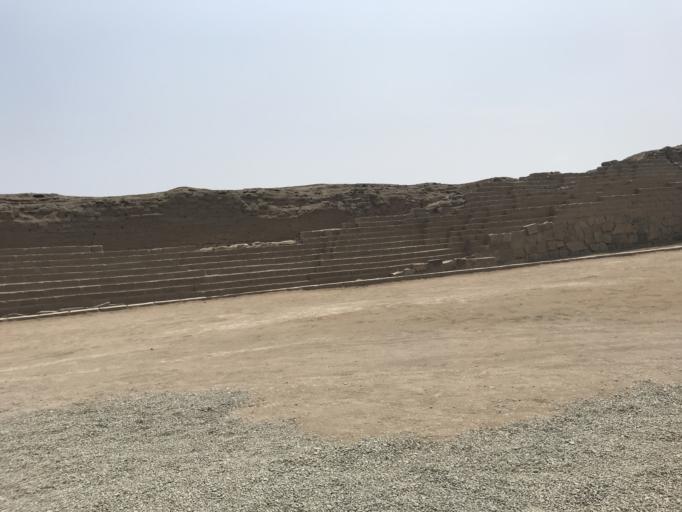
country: PE
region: Lima
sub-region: Lima
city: Punta Hermosa
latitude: -12.2564
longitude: -76.9021
